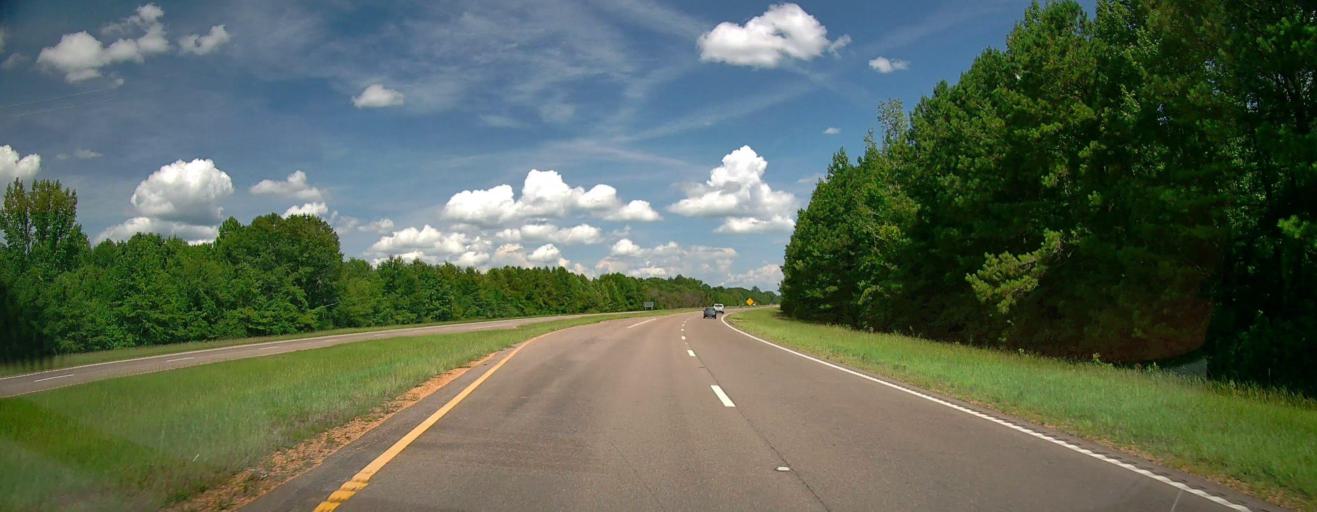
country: US
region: Mississippi
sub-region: Monroe County
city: Aberdeen
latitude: 33.8193
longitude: -88.5080
